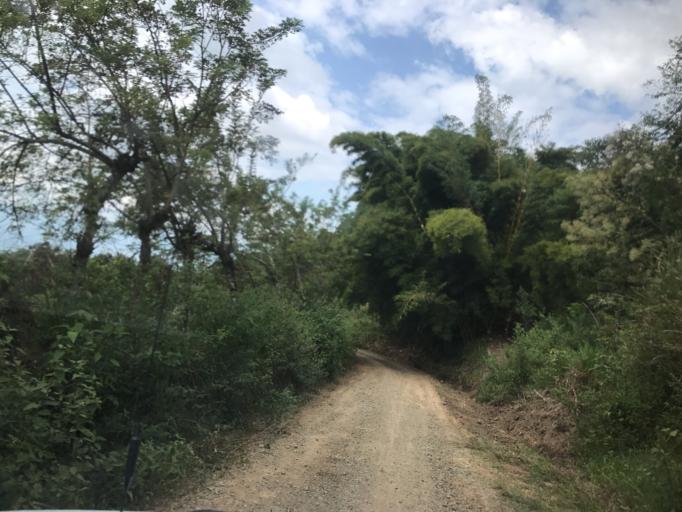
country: CO
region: Valle del Cauca
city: Obando
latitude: 4.5539
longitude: -75.9234
